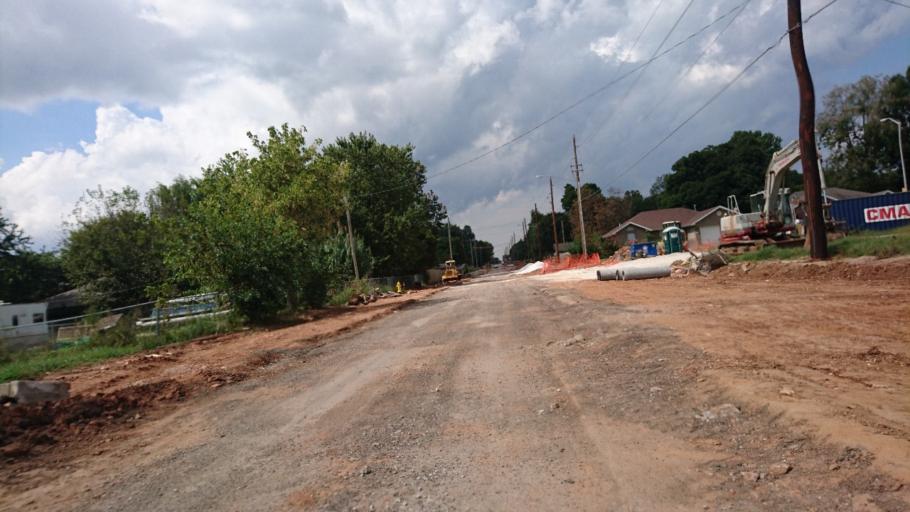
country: US
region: Missouri
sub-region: Greene County
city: Springfield
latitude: 37.2049
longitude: -93.3525
